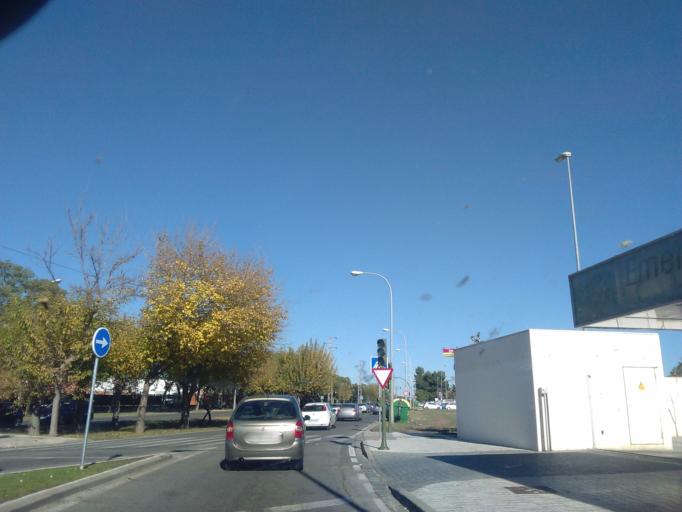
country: ES
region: Andalusia
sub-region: Provincia de Sevilla
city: Sevilla
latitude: 37.3869
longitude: -5.9166
